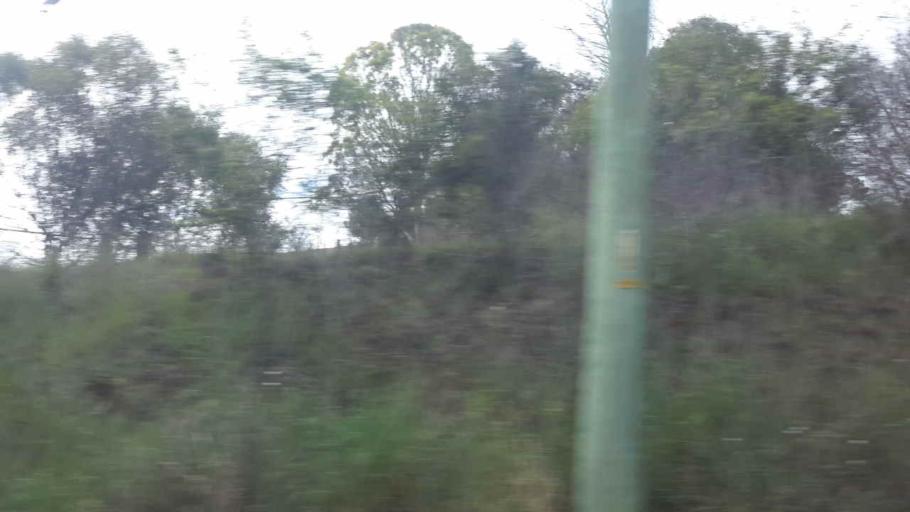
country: AU
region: New South Wales
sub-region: Camden
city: Camden South
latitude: -34.1275
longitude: 150.7188
